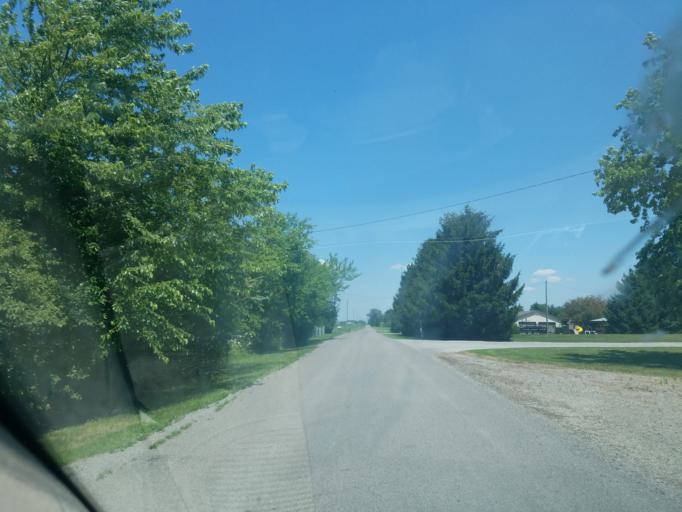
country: US
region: Ohio
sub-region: Allen County
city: Spencerville
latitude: 40.7636
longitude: -84.3494
